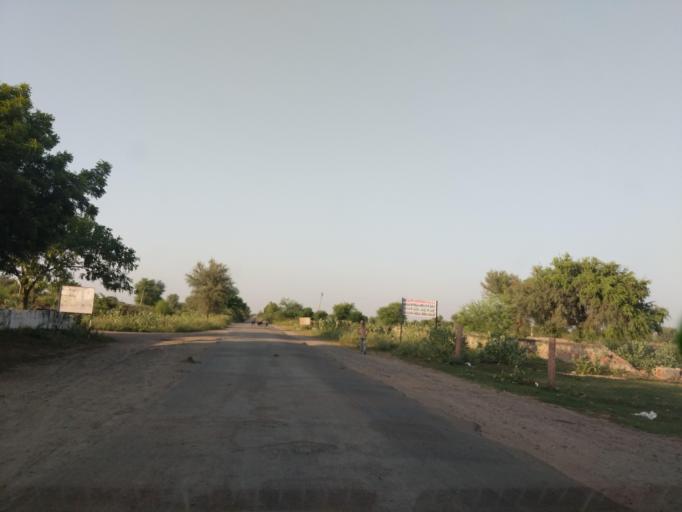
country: IN
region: Rajasthan
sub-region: Churu
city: Rajgarh
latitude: 28.5658
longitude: 75.3670
